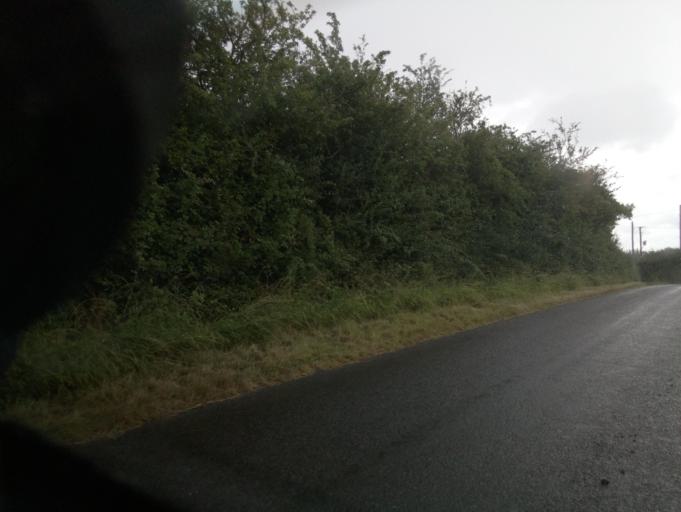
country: GB
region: England
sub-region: Worcestershire
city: Pershore
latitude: 52.1754
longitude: -2.1159
